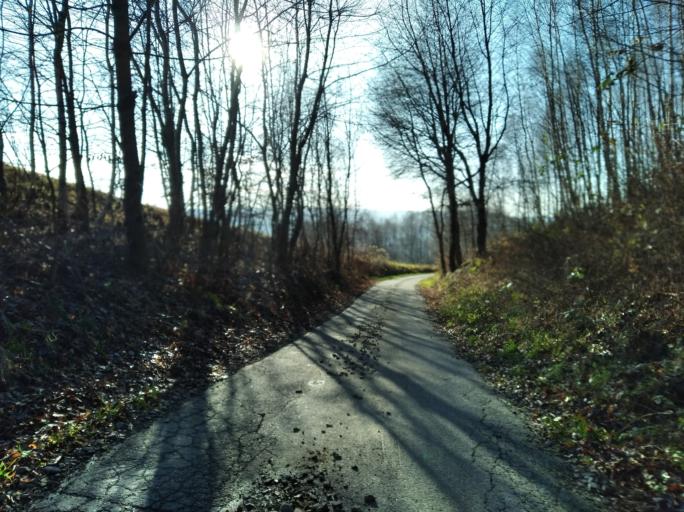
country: PL
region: Subcarpathian Voivodeship
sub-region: Powiat strzyzowski
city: Strzyzow
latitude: 49.8792
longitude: 21.8301
